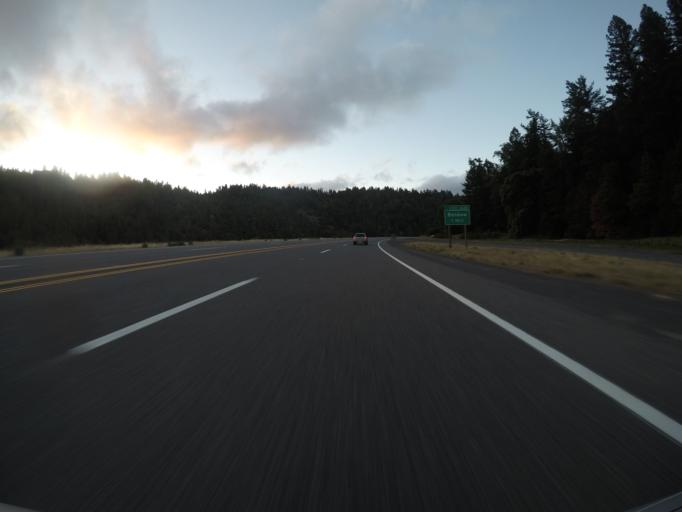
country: US
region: California
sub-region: Humboldt County
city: Redway
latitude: 40.0526
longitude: -123.7927
